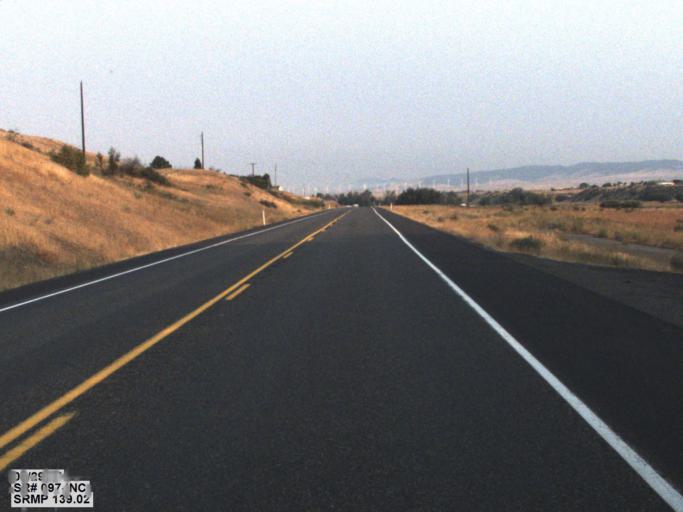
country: US
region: Washington
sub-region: Kittitas County
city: Ellensburg
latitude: 47.0679
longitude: -120.6248
